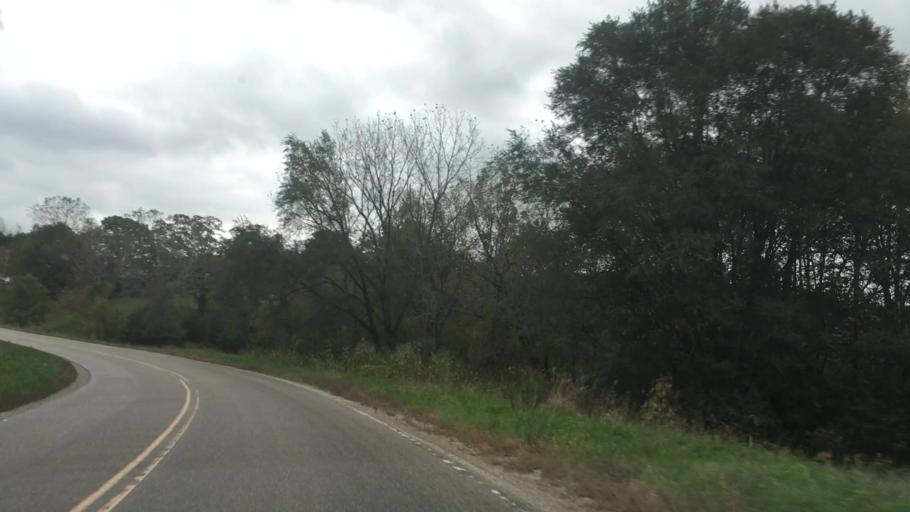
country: US
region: Minnesota
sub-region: Fillmore County
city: Preston
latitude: 43.7424
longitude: -92.0164
